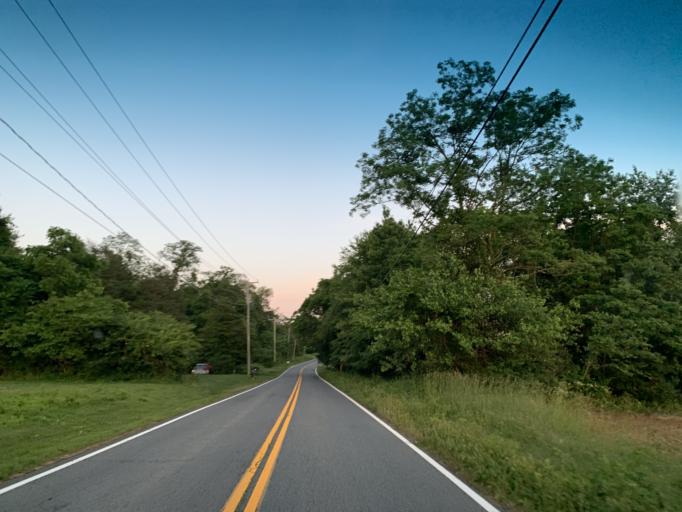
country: US
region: Maryland
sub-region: Cecil County
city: Perryville
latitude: 39.6258
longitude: -76.0717
